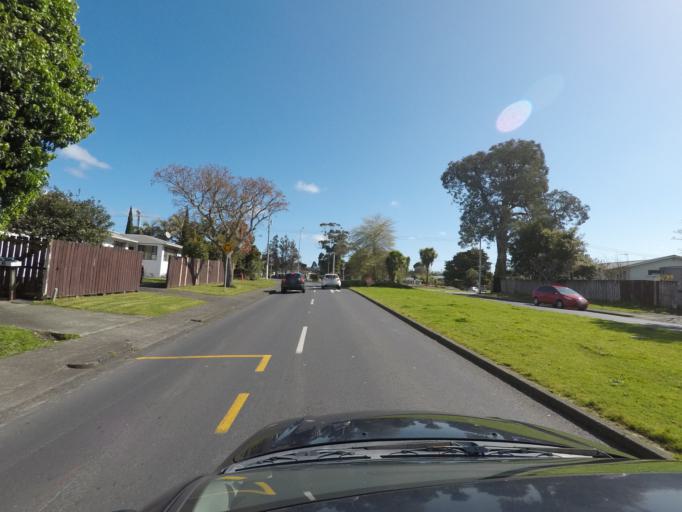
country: NZ
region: Auckland
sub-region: Auckland
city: Rosebank
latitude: -36.8605
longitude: 174.6126
